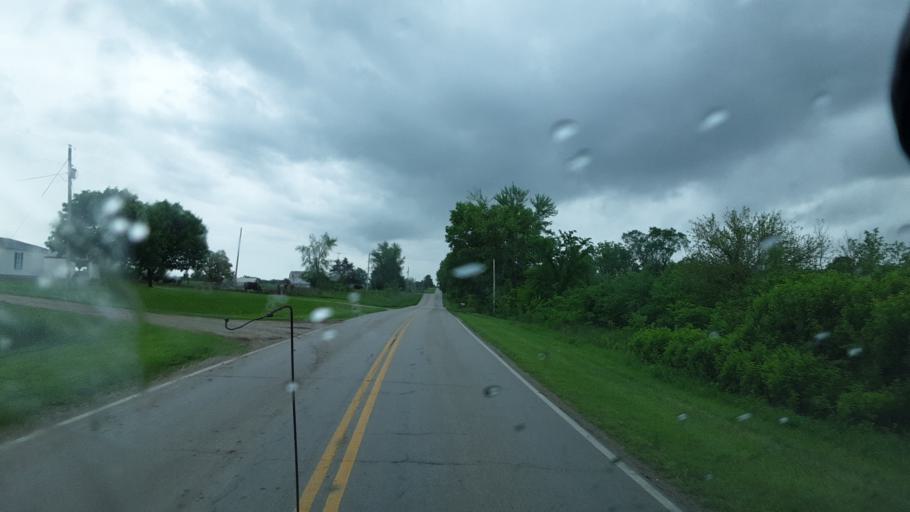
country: US
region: Missouri
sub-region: Monroe County
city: Paris
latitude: 39.4437
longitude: -92.2085
